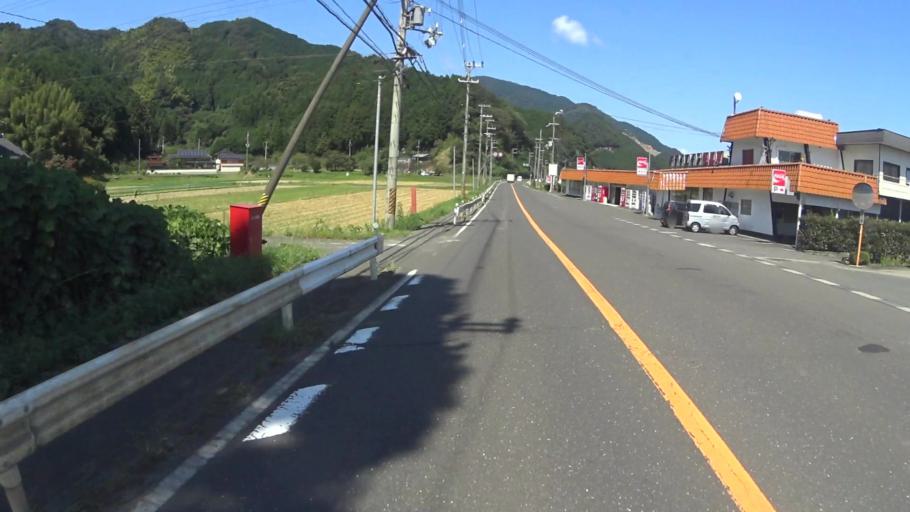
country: JP
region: Kyoto
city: Maizuru
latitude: 35.4700
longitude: 135.2776
